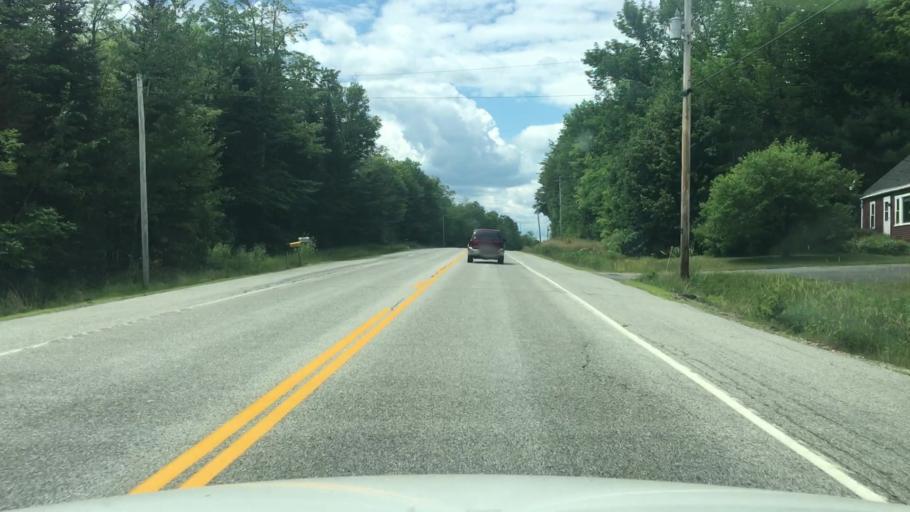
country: US
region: Maine
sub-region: Oxford County
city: West Paris
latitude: 44.3675
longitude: -70.5958
